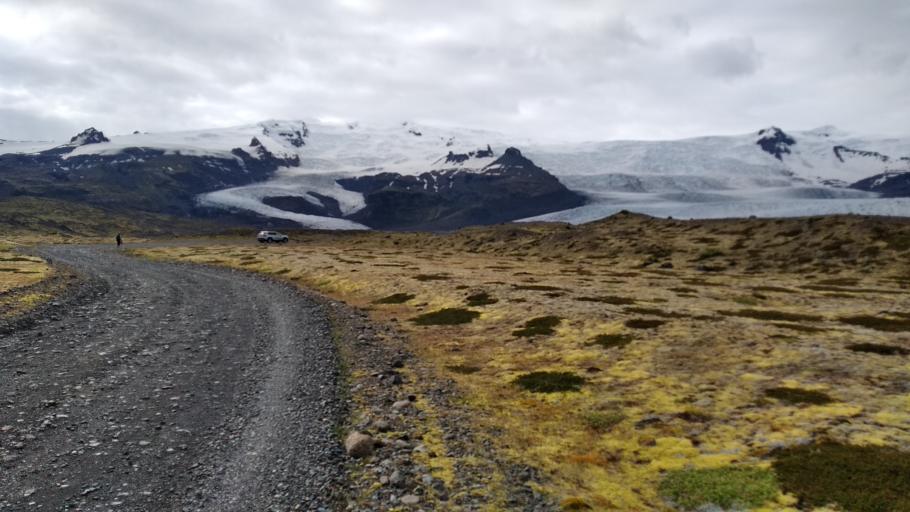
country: IS
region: East
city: Hoefn
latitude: 64.0112
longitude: -16.3865
